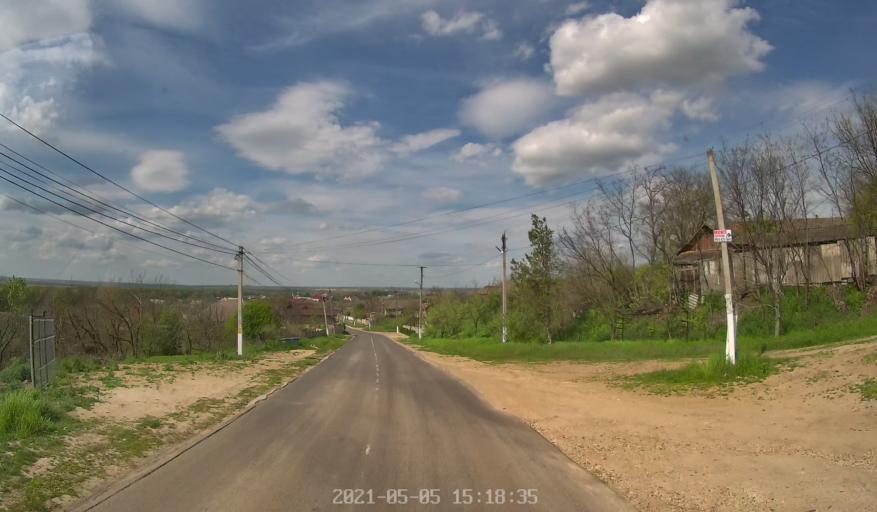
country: MD
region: Criuleni
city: Criuleni
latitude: 47.1208
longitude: 29.1946
